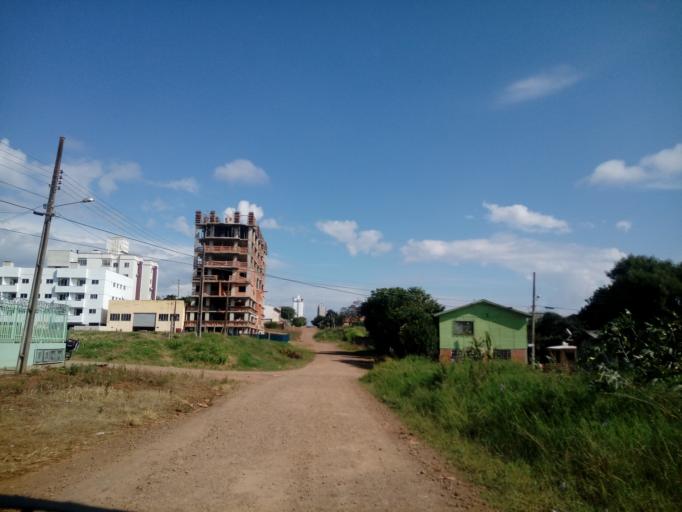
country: BR
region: Santa Catarina
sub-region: Chapeco
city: Chapeco
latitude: -27.0991
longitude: -52.5975
